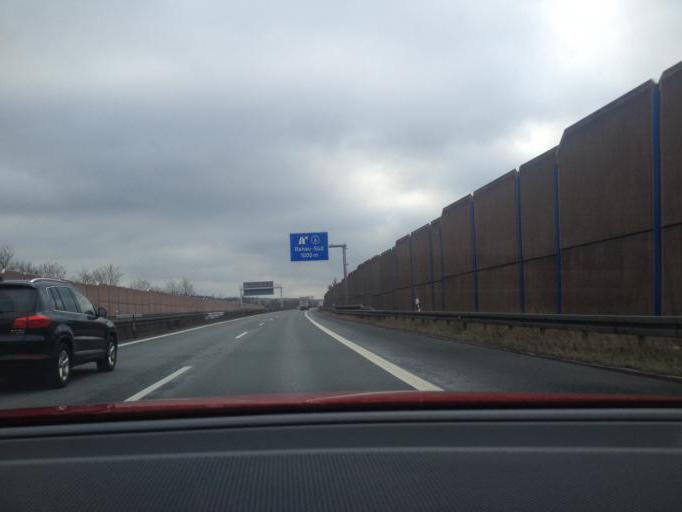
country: DE
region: Bavaria
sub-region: Upper Franconia
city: Rehau
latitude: 50.2563
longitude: 12.0516
